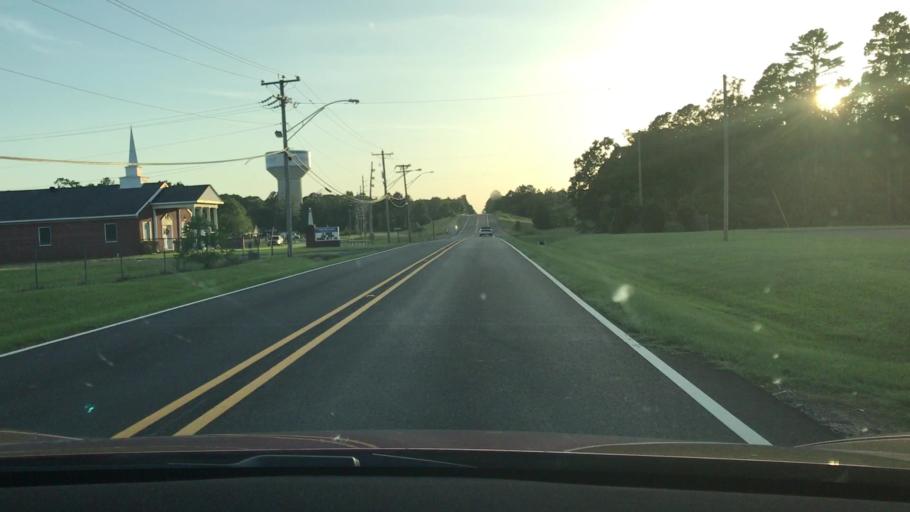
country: US
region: Louisiana
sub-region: Bossier Parish
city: Bossier City
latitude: 32.3909
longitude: -93.7473
